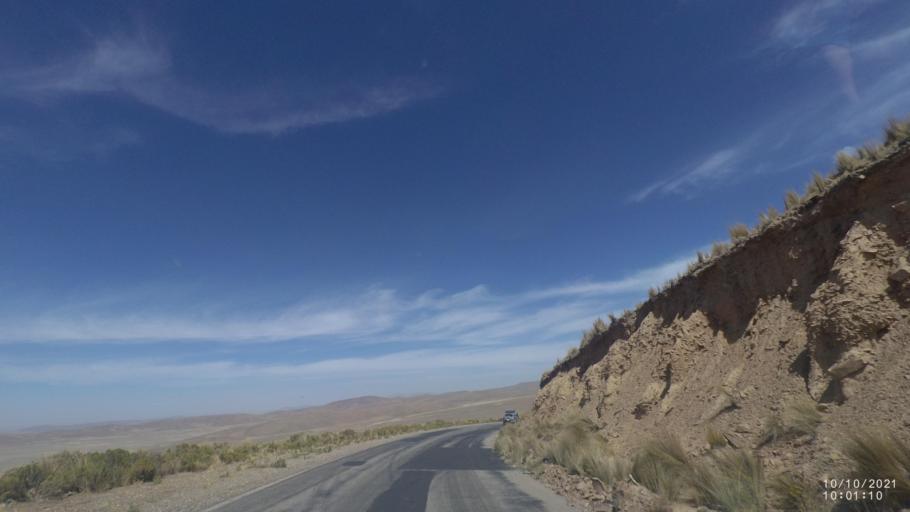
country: BO
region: La Paz
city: Eucaliptus
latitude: -17.3671
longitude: -67.4195
